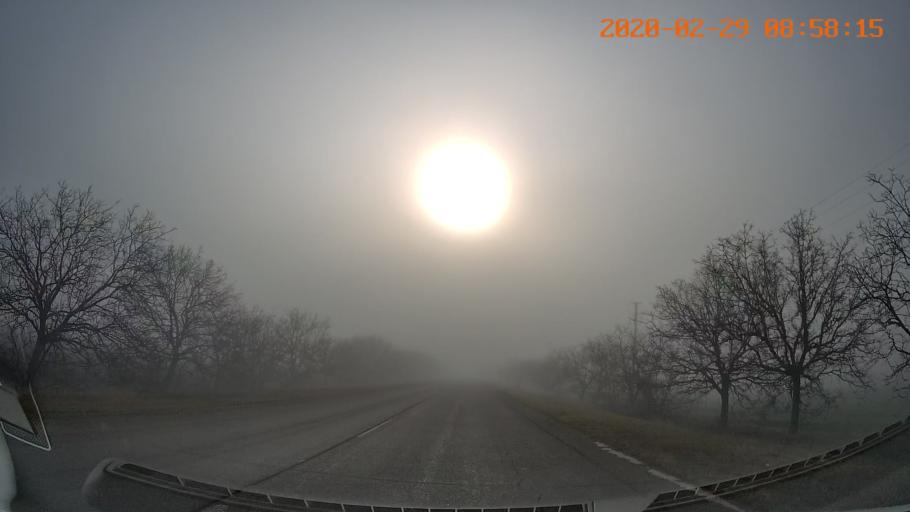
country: MD
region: Telenesti
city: Tiraspolul Nou
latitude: 46.9221
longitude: 29.6382
